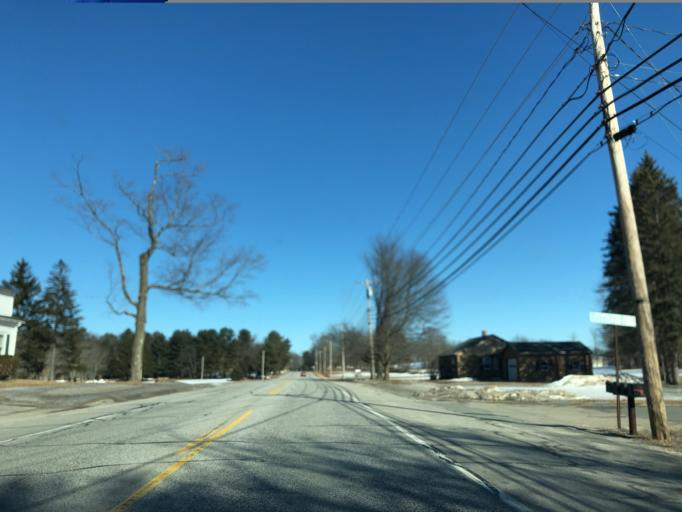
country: US
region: Maine
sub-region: Cumberland County
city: North Windham
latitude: 43.7958
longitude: -70.4077
